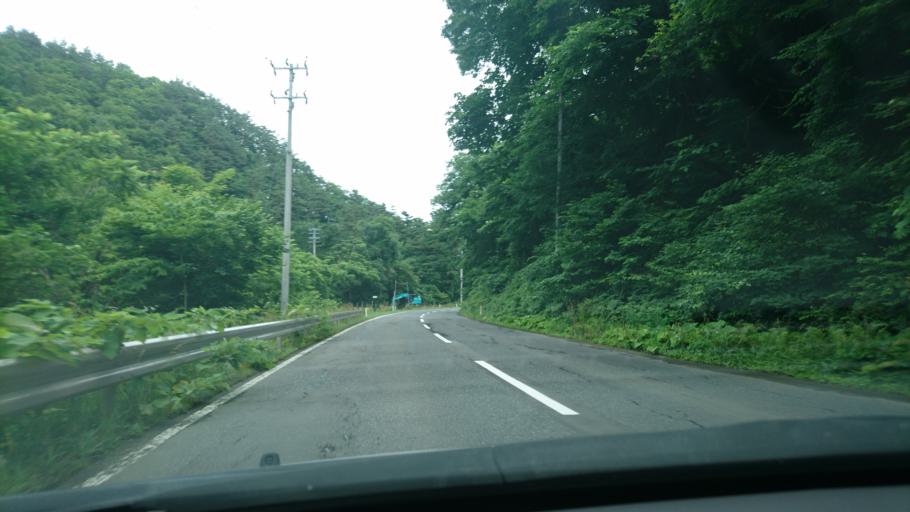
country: JP
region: Iwate
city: Miyako
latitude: 39.9901
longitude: 141.8724
